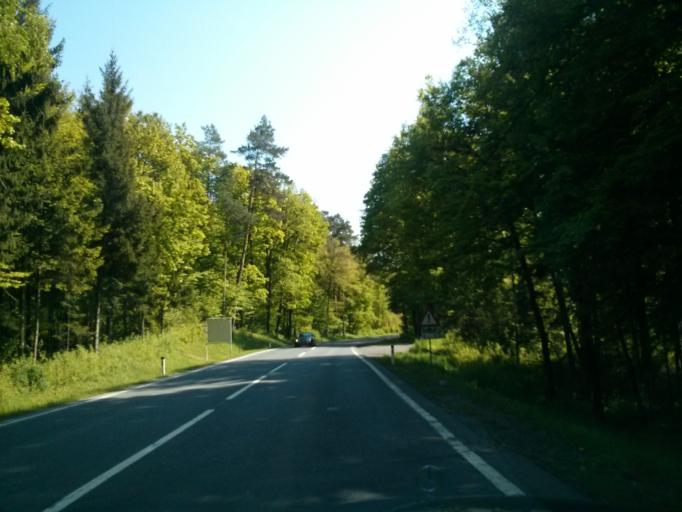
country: AT
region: Burgenland
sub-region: Politischer Bezirk Oberwart
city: Bad Tatzmannsdorf
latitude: 47.3332
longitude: 16.2203
